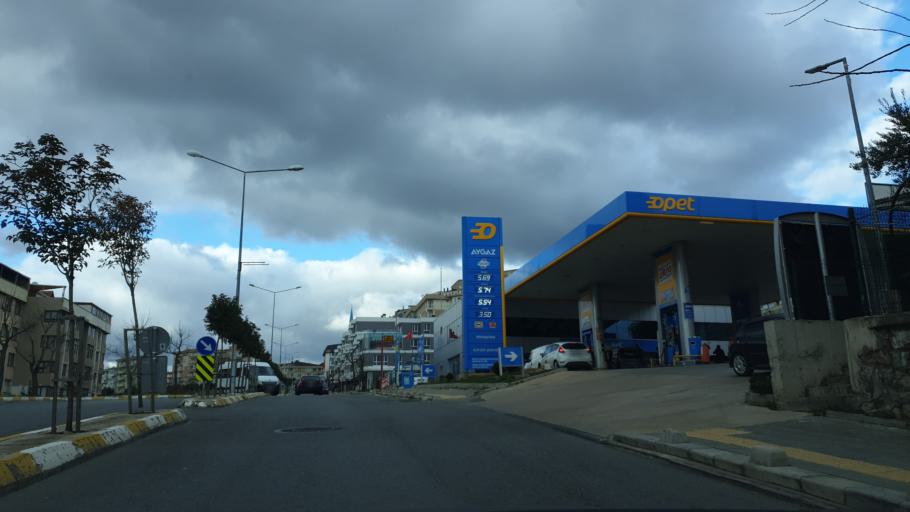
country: TR
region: Istanbul
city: Pendik
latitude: 40.9013
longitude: 29.2468
